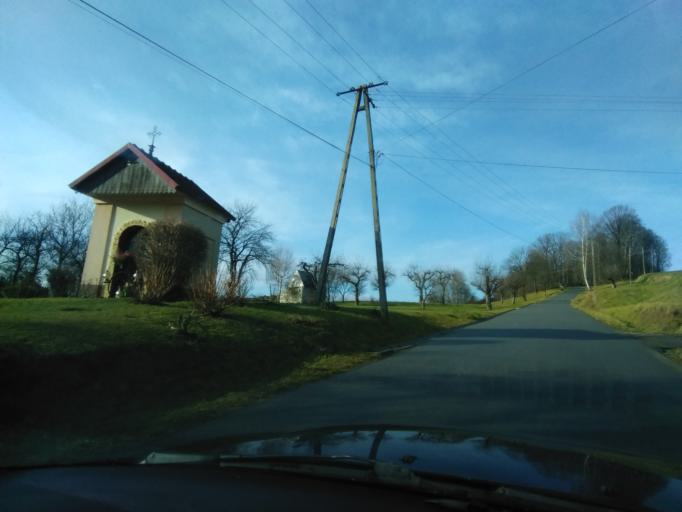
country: PL
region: Subcarpathian Voivodeship
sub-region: Powiat krosnienski
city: Korczyna
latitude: 49.7243
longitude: 21.7999
